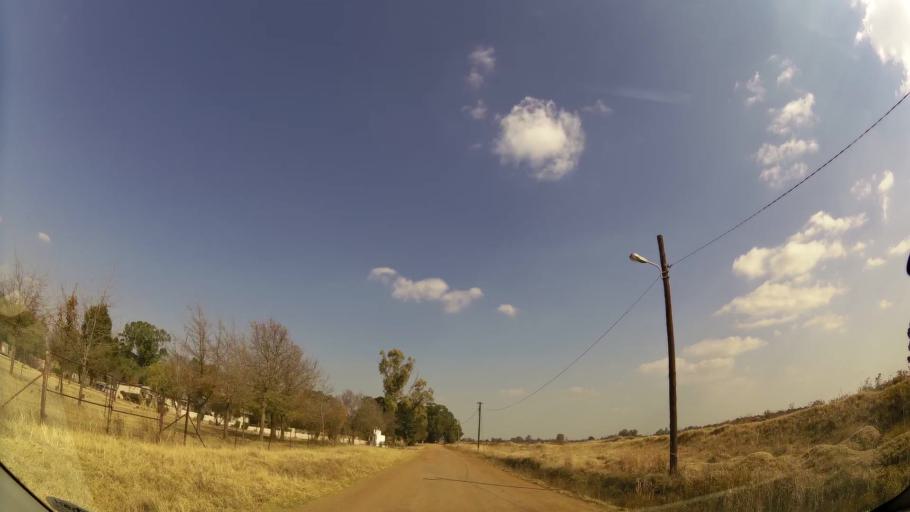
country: ZA
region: Gauteng
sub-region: Ekurhuleni Metropolitan Municipality
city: Benoni
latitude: -26.1014
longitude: 28.4074
